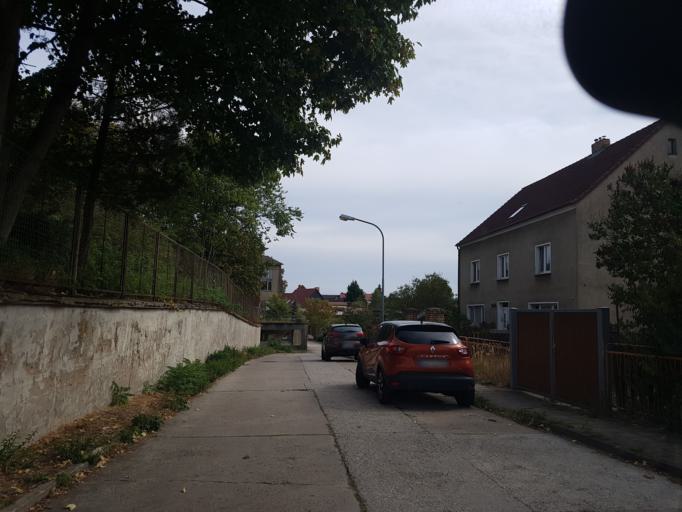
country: DE
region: Brandenburg
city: Wiesenburg
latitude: 52.1156
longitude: 12.4510
